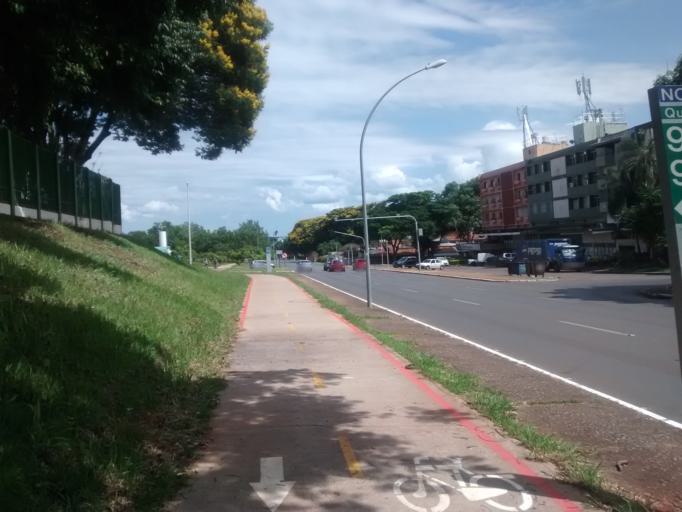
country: BR
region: Federal District
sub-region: Brasilia
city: Brasilia
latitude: -15.7649
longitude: -47.8938
